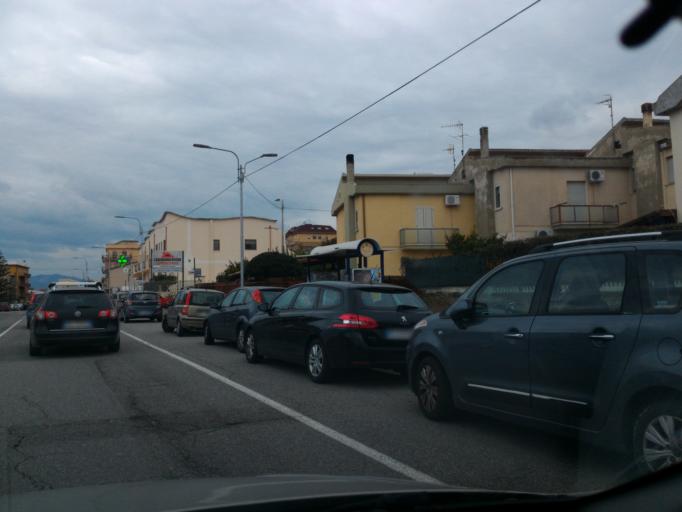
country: IT
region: Calabria
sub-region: Provincia di Catanzaro
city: Barone
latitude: 38.8321
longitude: 16.6310
